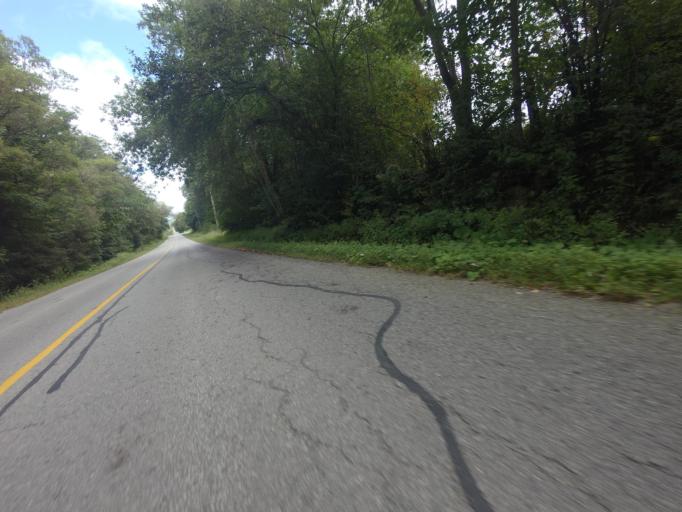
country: CA
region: Ontario
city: Uxbridge
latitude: 44.1235
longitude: -79.1427
